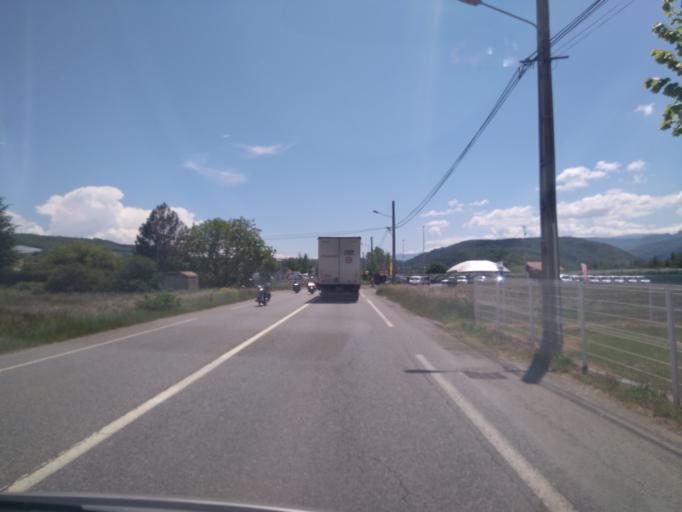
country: FR
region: Provence-Alpes-Cote d'Azur
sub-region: Departement des Hautes-Alpes
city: Laragne-Monteglin
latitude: 44.3057
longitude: 5.8359
